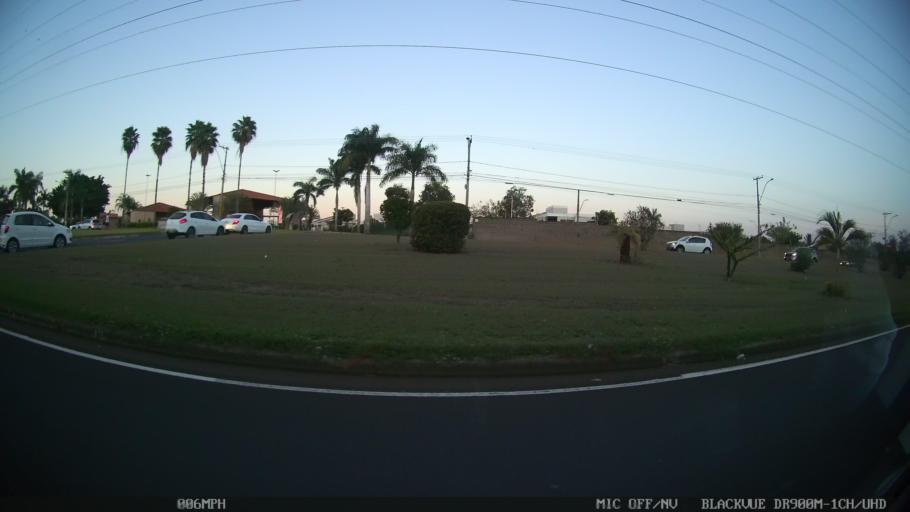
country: BR
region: Sao Paulo
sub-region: Sao Jose Do Rio Preto
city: Sao Jose do Rio Preto
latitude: -20.8177
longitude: -49.3390
